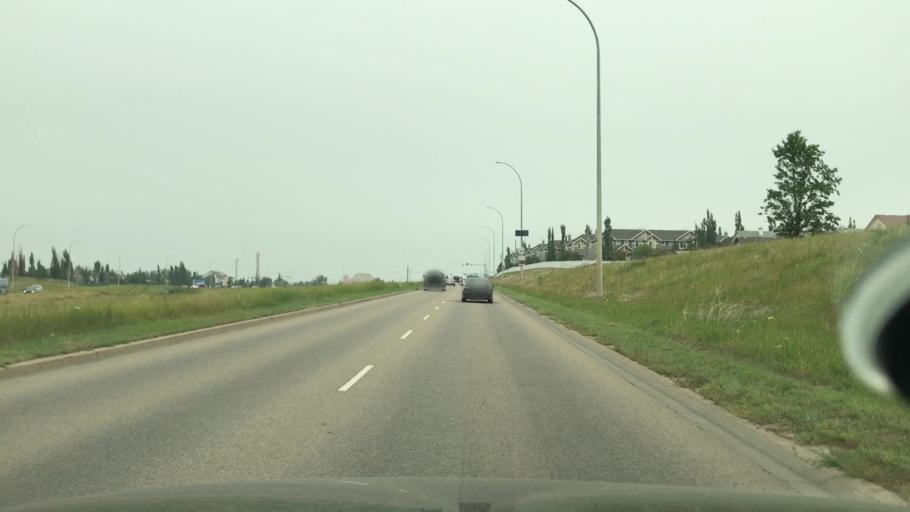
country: CA
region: Alberta
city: Edmonton
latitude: 53.4532
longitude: -113.5892
